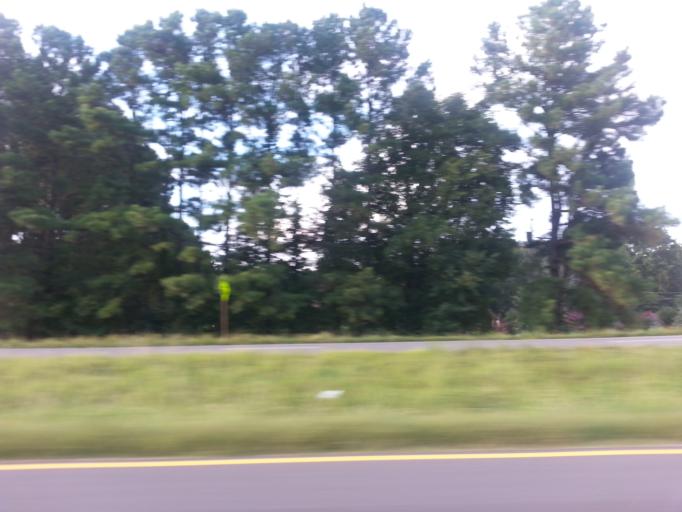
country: US
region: Alabama
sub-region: Madison County
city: Madison
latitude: 34.7485
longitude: -86.7927
